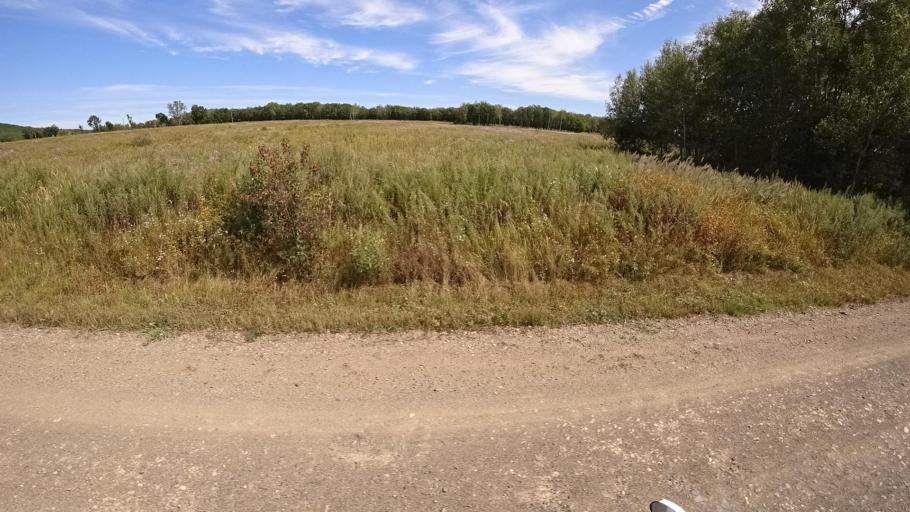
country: RU
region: Primorskiy
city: Yakovlevka
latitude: 44.7173
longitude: 133.6174
